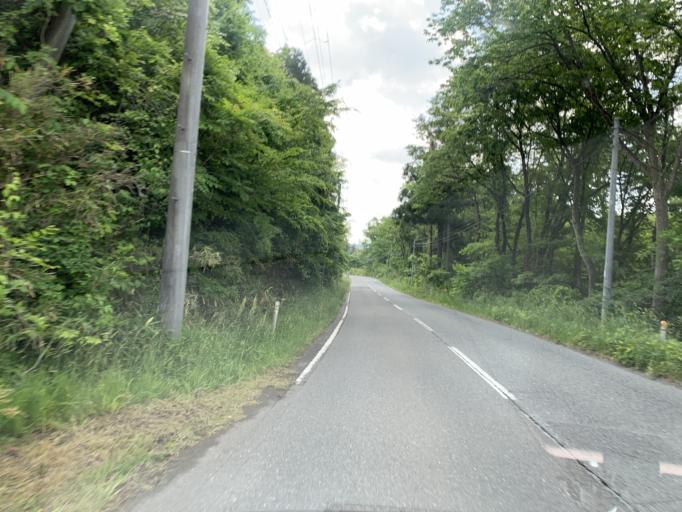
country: JP
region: Miyagi
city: Furukawa
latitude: 38.7751
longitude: 140.9606
